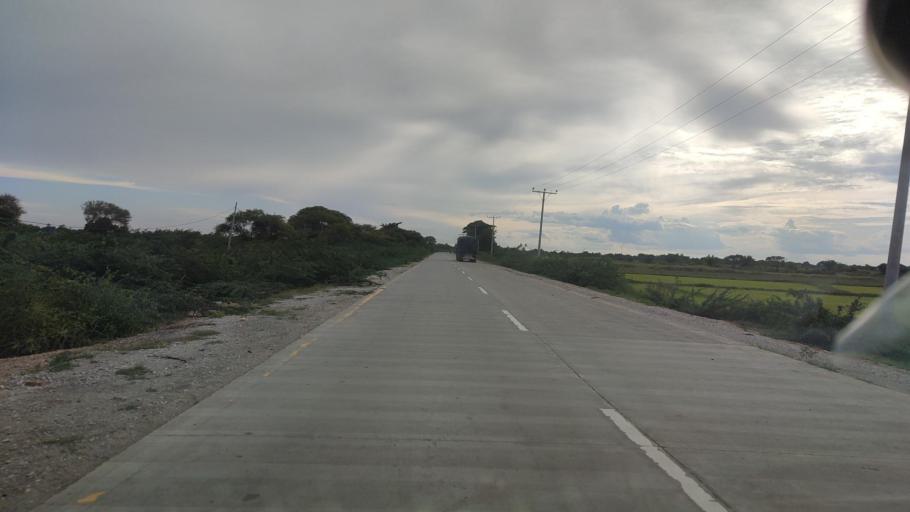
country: MM
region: Mandalay
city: Kyaukse
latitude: 21.3283
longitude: 96.0371
